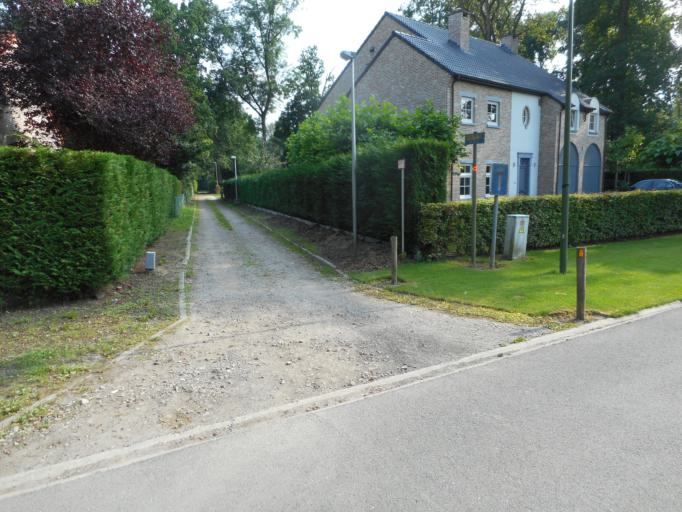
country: BE
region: Flanders
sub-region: Provincie Vlaams-Brabant
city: Kampenhout
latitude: 50.9347
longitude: 4.5557
